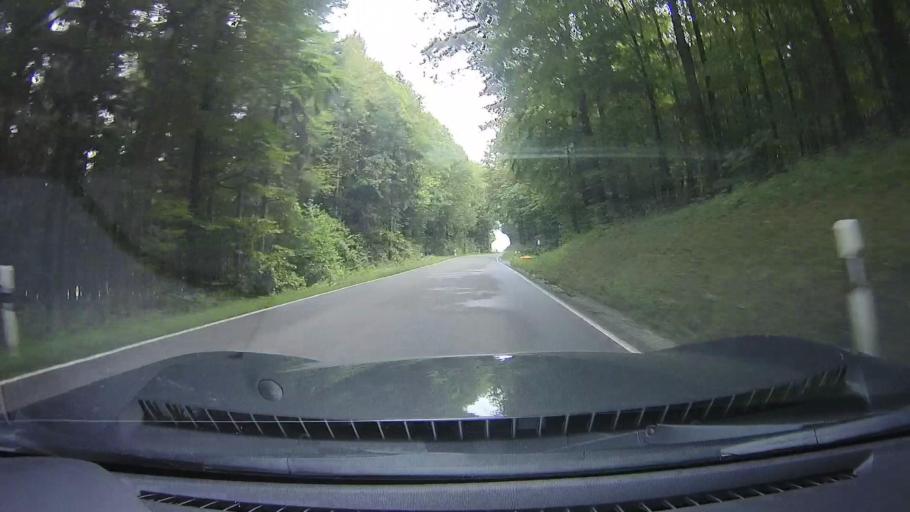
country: DE
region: Baden-Wuerttemberg
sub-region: Regierungsbezirk Stuttgart
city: Lowenstein
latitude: 49.0478
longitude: 9.3974
